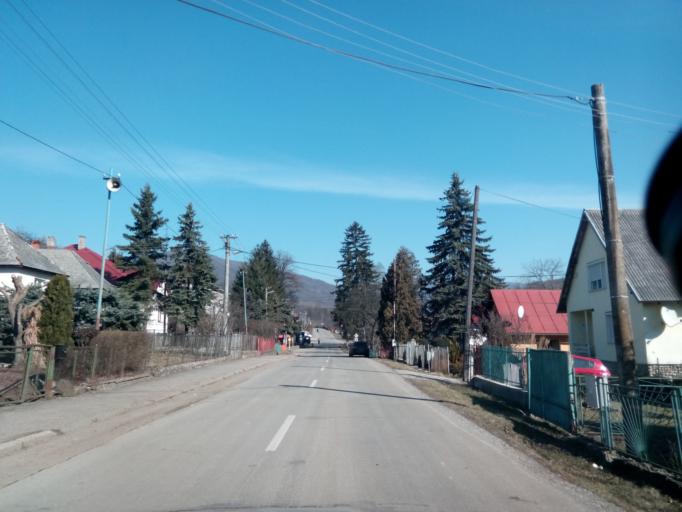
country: SK
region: Kosicky
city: Sobrance
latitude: 48.8475
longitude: 22.1837
